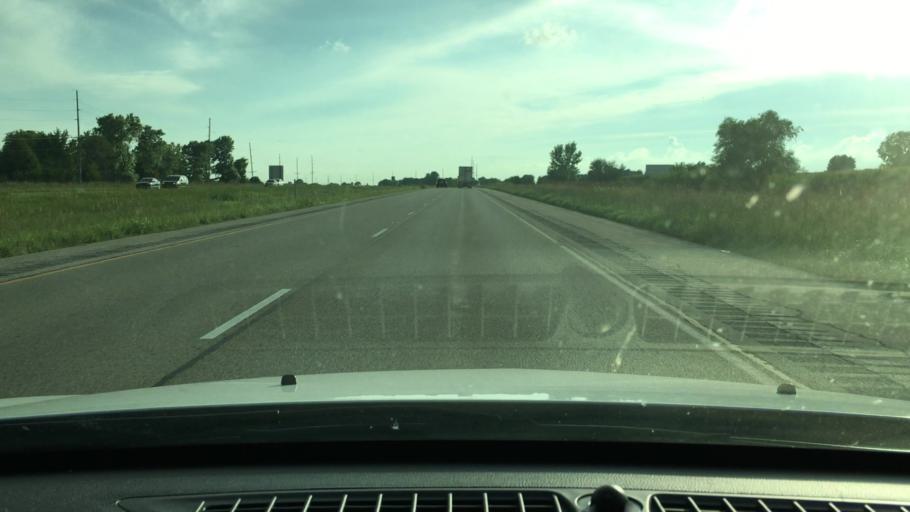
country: US
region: Illinois
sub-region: Logan County
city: Atlanta
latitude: 40.3059
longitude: -89.1754
